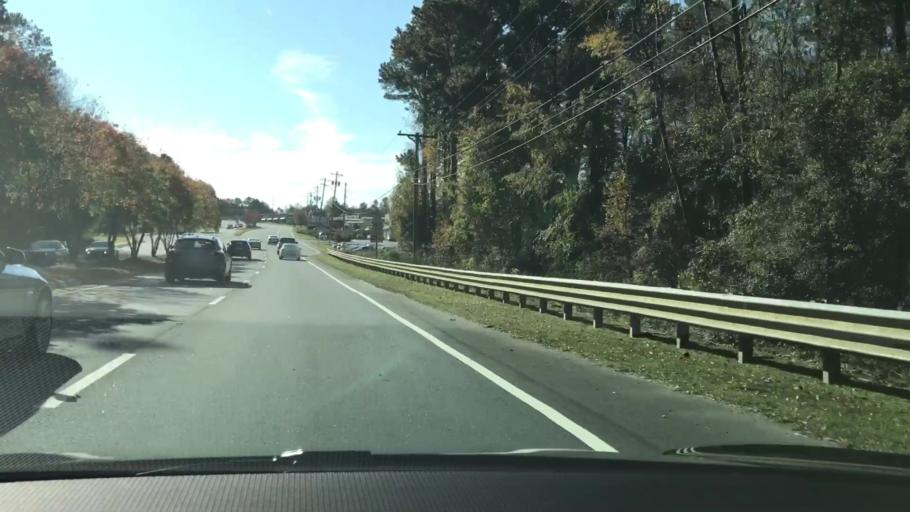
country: US
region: Georgia
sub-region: Gwinnett County
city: Suwanee
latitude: 34.0506
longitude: -84.0599
